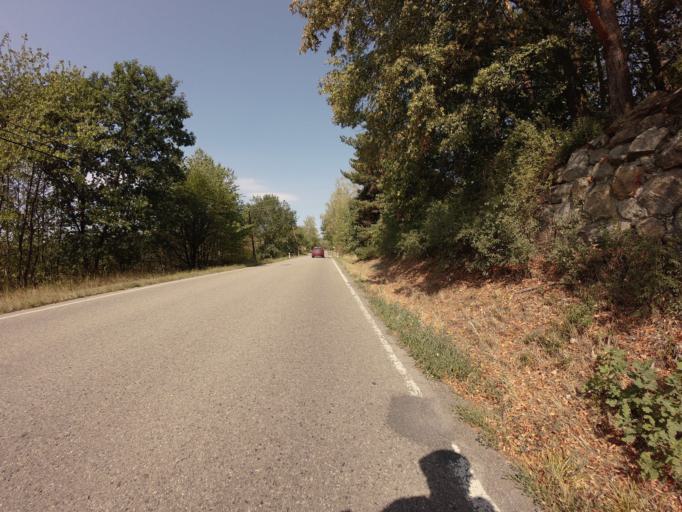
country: CZ
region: Central Bohemia
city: Kamenny Privoz
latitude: 49.8615
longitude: 14.5375
